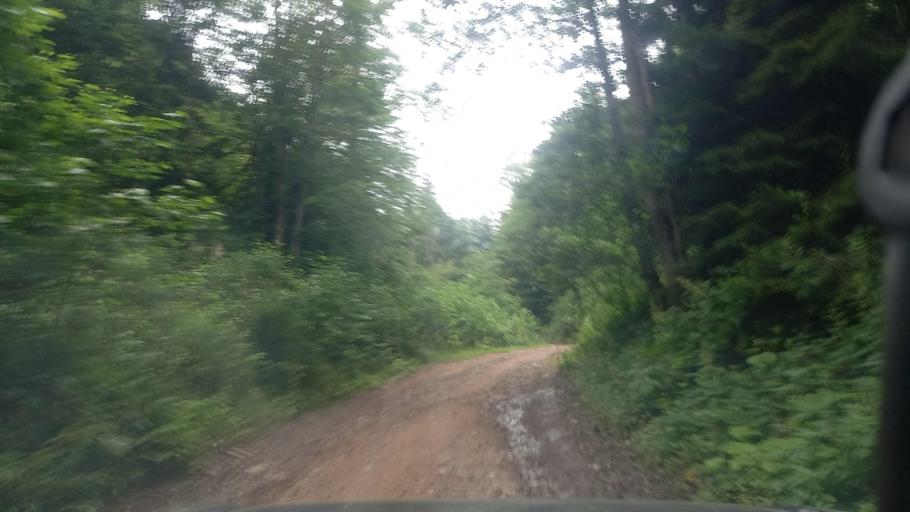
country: RU
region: Karachayevo-Cherkesiya
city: Kurdzhinovo
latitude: 43.8124
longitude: 40.8744
